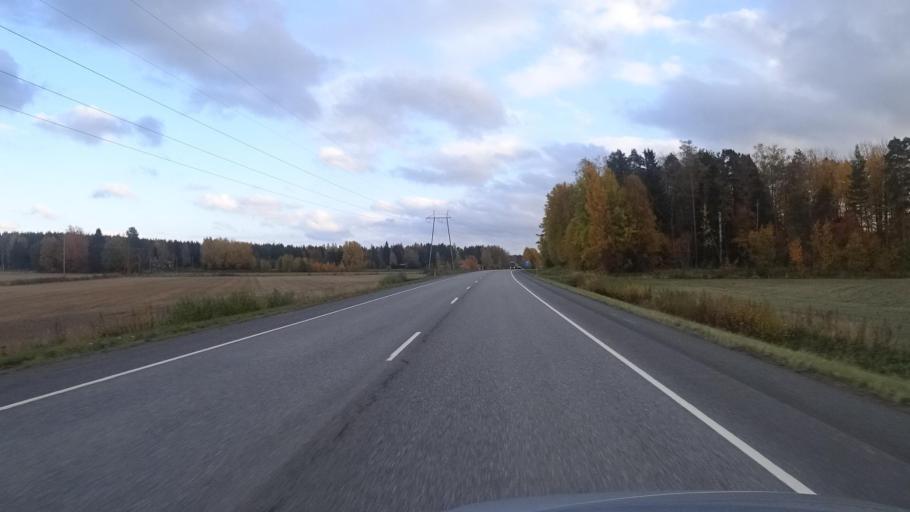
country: FI
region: Satakunta
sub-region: Rauma
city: Saekylae
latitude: 61.0264
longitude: 22.4020
